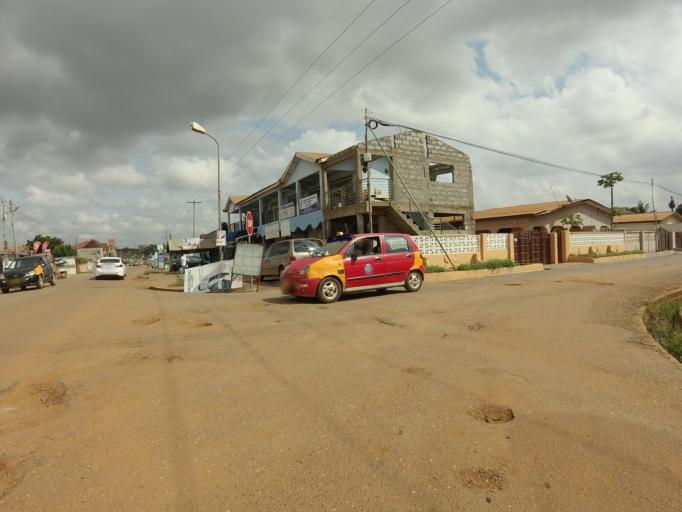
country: GH
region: Greater Accra
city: Teshi Old Town
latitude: 5.6111
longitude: -0.1062
